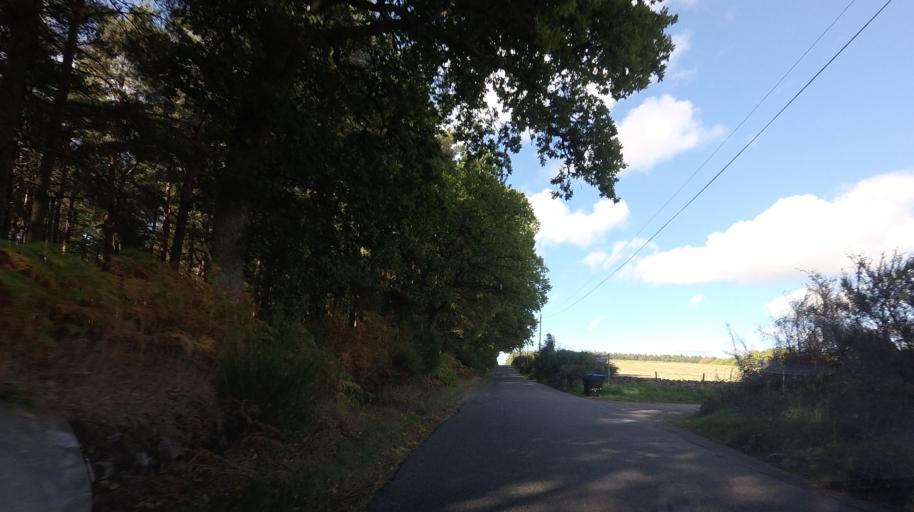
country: GB
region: Scotland
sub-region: Aberdeenshire
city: Banchory
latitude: 57.0673
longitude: -2.4678
